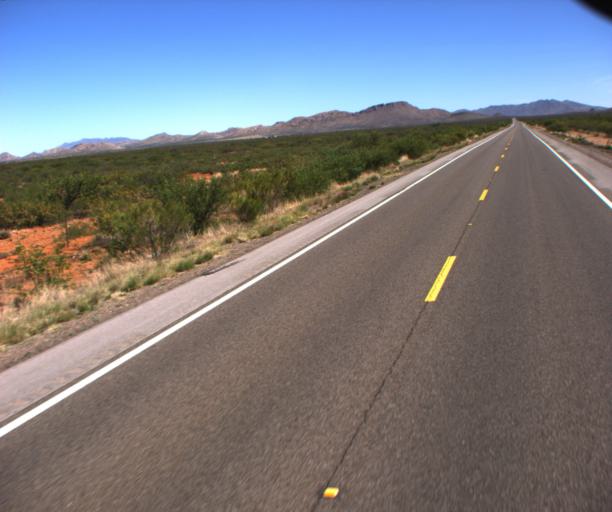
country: US
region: Arizona
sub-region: Cochise County
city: Douglas
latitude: 31.4159
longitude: -109.4938
